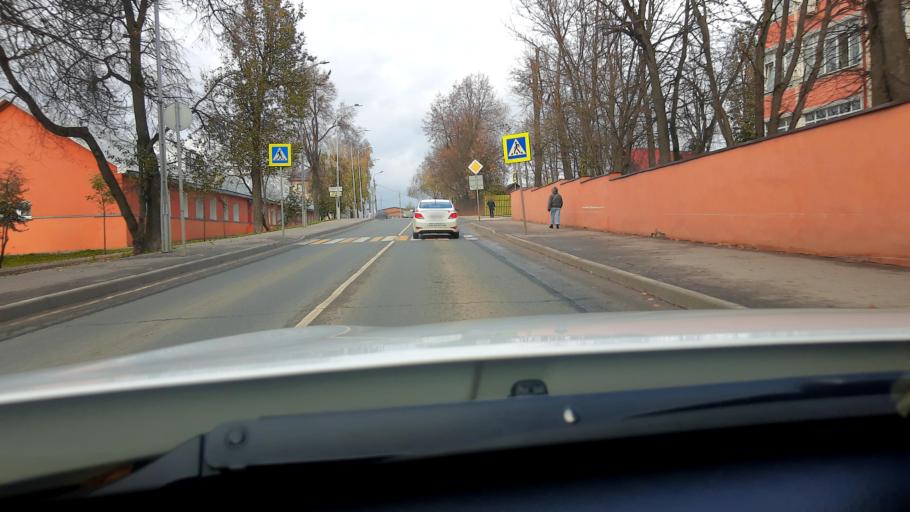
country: RU
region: Moskovskaya
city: Kokoshkino
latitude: 55.5370
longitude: 37.1531
